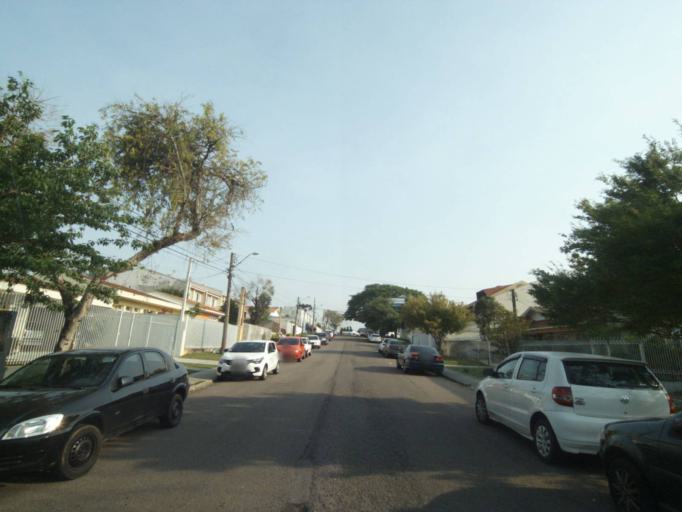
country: BR
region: Parana
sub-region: Curitiba
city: Curitiba
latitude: -25.4648
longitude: -49.2997
